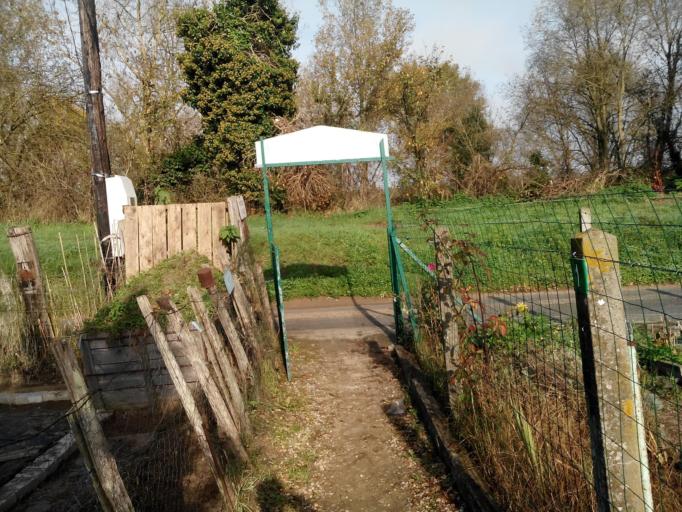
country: FR
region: Centre
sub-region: Departement d'Indre-et-Loire
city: Saint-Cyr-sur-Loire
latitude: 47.3869
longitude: 0.6372
